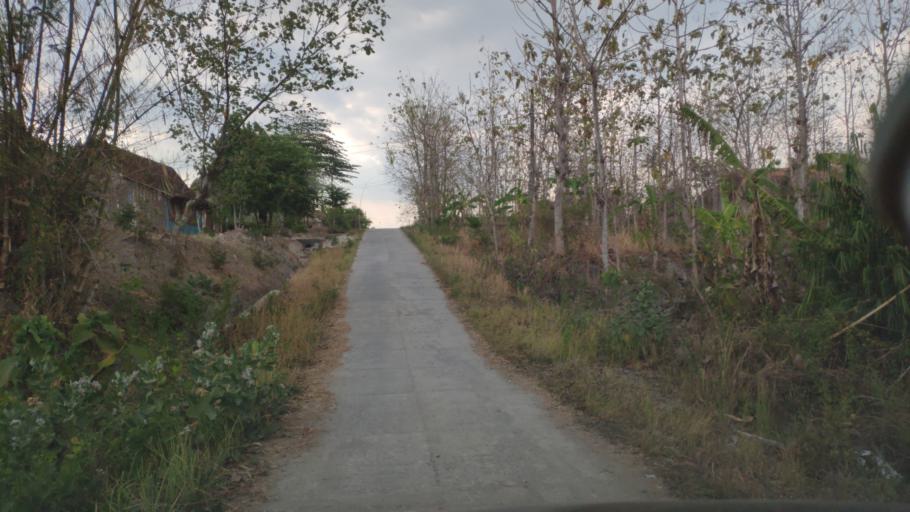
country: ID
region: Central Java
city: Randublatung
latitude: -7.2905
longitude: 111.3139
